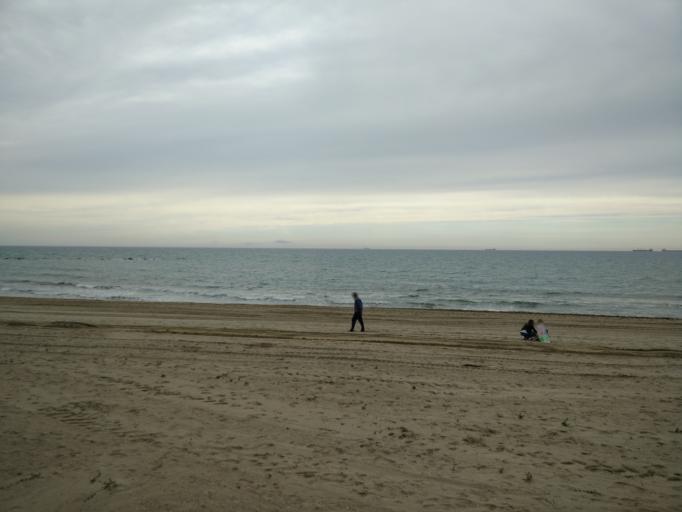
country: ES
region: Valencia
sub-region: Provincia de Castello
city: Benicassim
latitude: 40.0165
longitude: 0.0394
